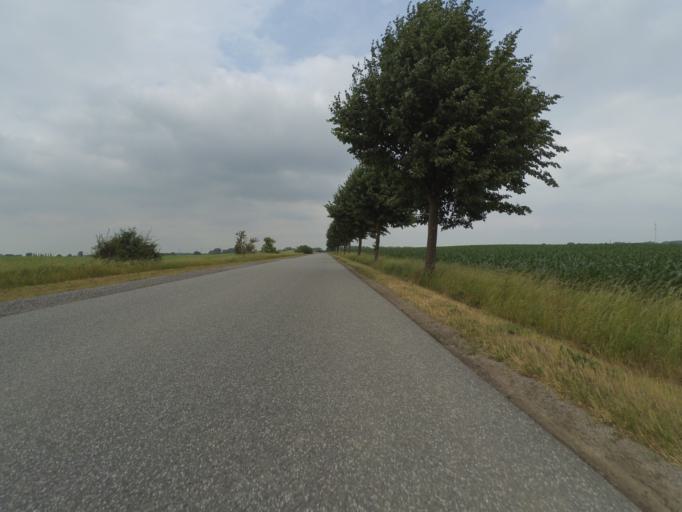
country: DE
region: Mecklenburg-Vorpommern
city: Plau am See
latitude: 53.4484
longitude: 12.2363
